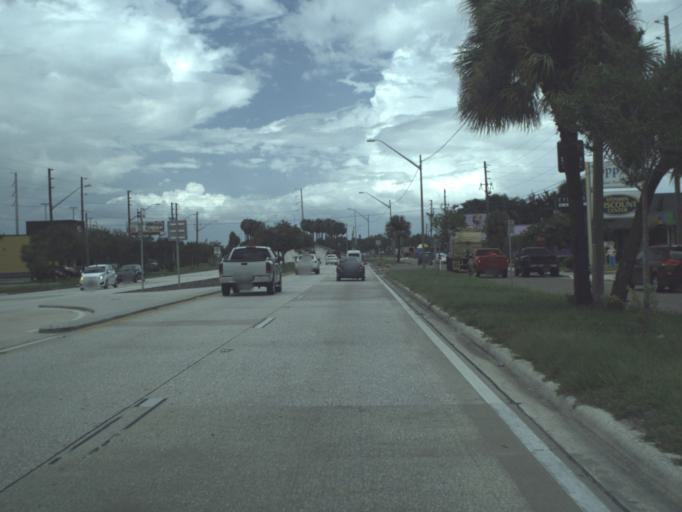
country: US
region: Florida
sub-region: Pinellas County
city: Kenneth City
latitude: 27.7965
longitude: -82.7335
